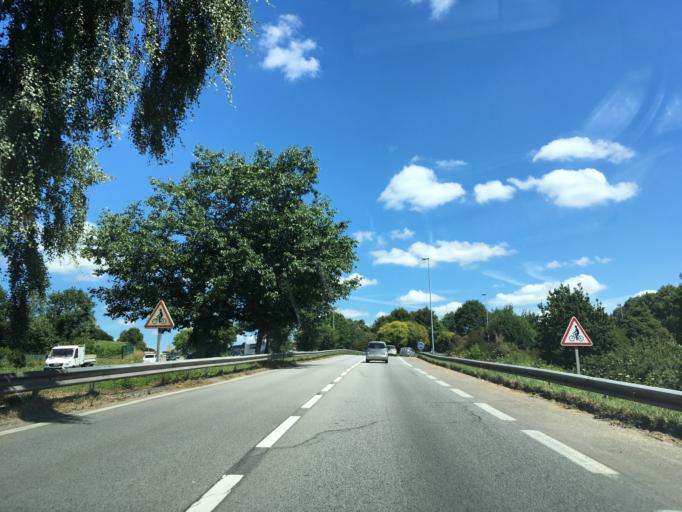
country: FR
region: Brittany
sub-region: Departement du Finistere
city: Quimper
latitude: 47.9800
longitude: -4.0823
